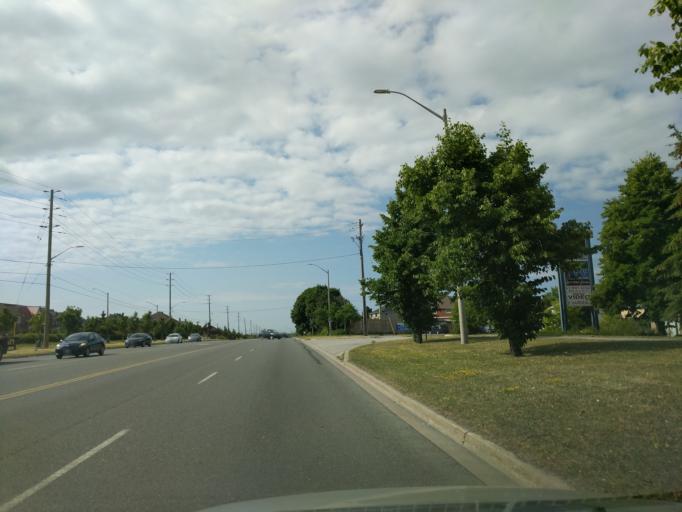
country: CA
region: Ontario
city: Markham
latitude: 43.8436
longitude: -79.2524
